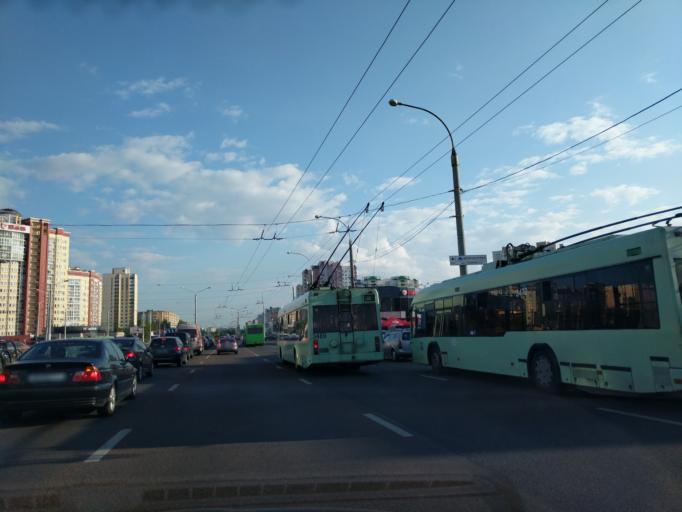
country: BY
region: Minsk
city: Novoye Medvezhino
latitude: 53.9083
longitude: 27.4358
